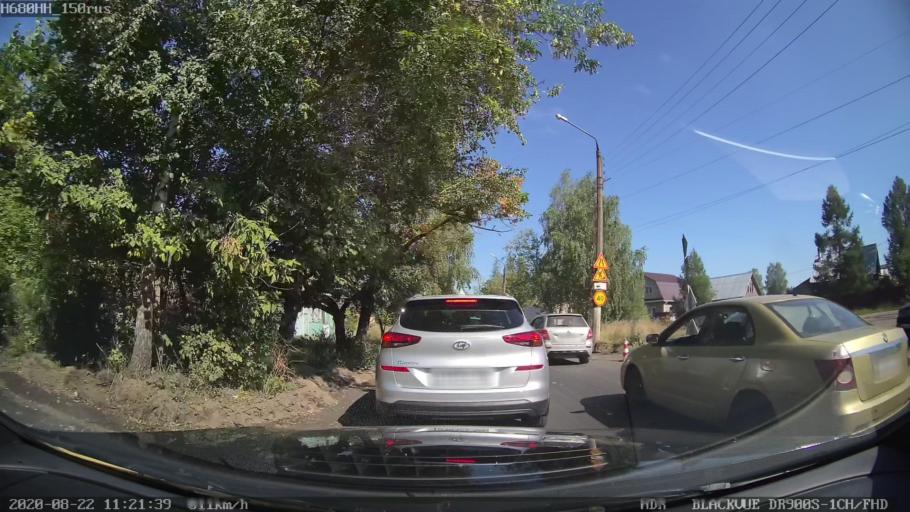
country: RU
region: Tverskaya
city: Tver
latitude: 56.8773
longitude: 35.9294
